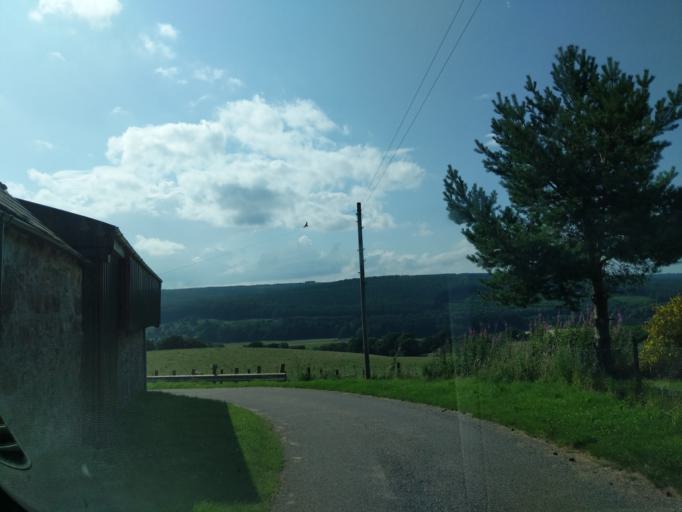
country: GB
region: Scotland
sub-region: Moray
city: Fochabers
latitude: 57.5587
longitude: -3.1302
